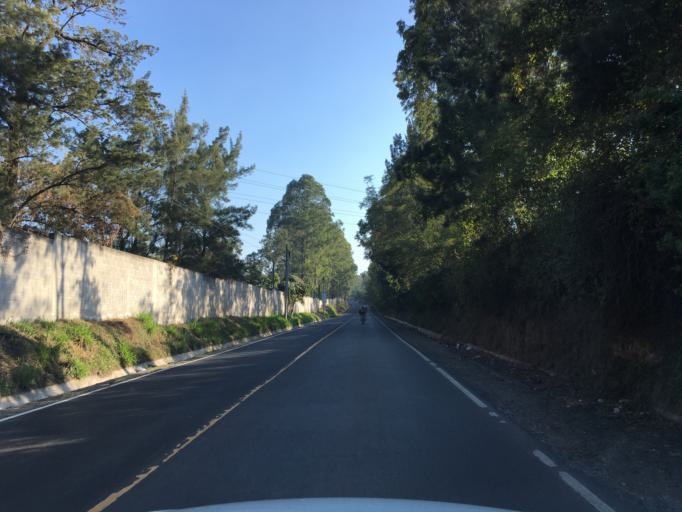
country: GT
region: Guatemala
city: Villa Nueva
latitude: 14.5240
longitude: -90.6168
